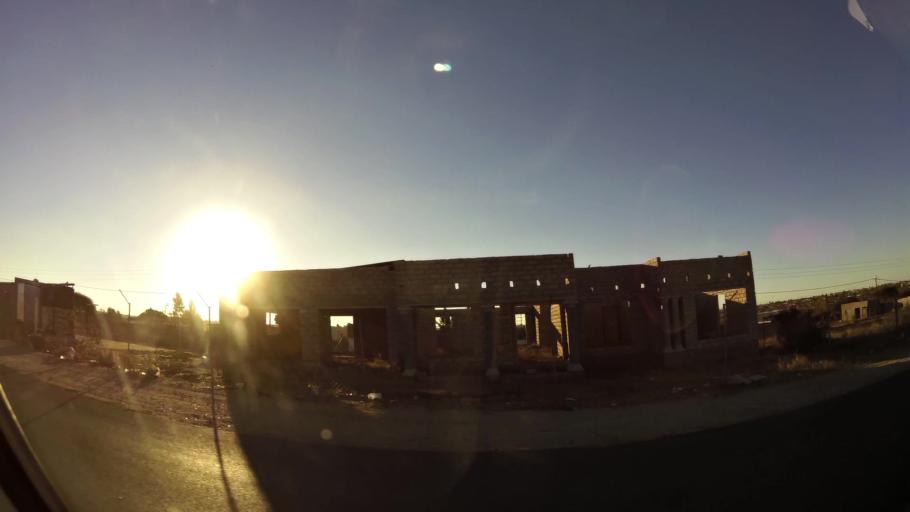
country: ZA
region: Limpopo
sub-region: Capricorn District Municipality
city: Polokwane
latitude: -23.8327
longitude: 29.3692
